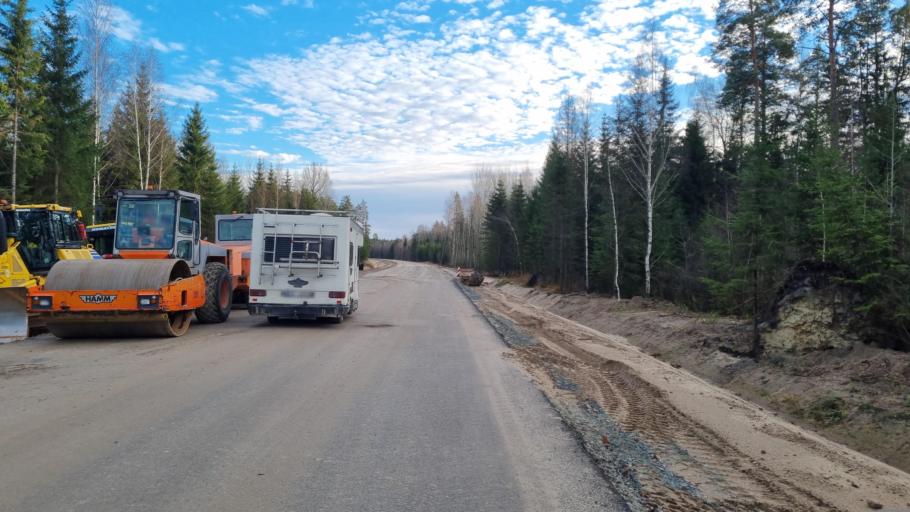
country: LV
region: Kekava
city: Kekava
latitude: 56.7949
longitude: 24.2106
